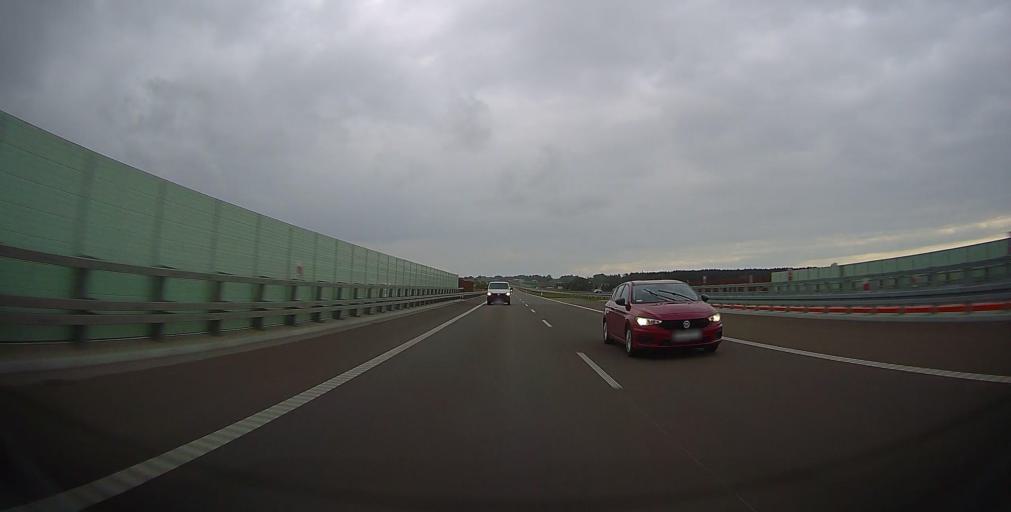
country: PL
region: Masovian Voivodeship
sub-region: Powiat radomski
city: Jedlinsk
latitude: 51.4978
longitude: 21.0766
